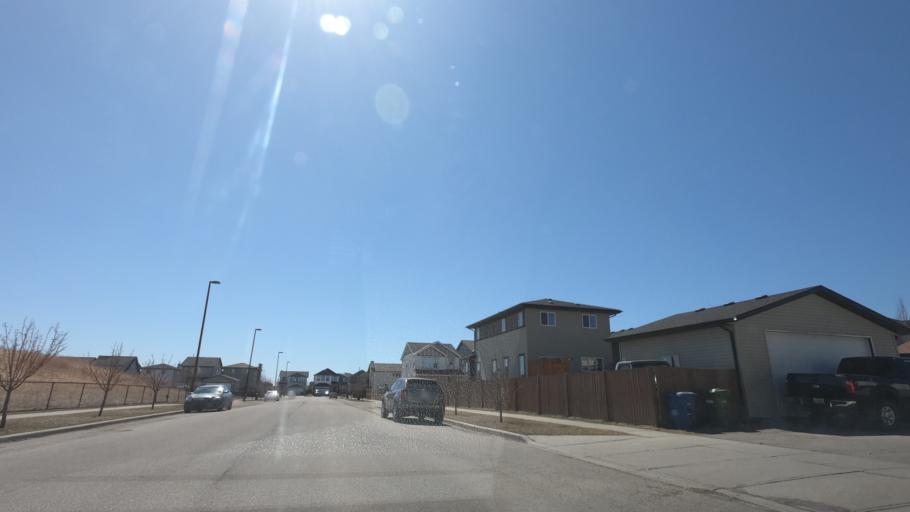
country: CA
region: Alberta
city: Airdrie
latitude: 51.3044
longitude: -114.0433
